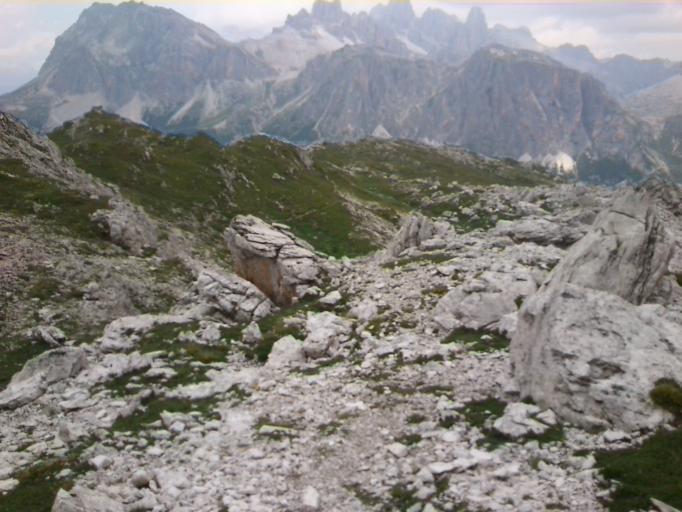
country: IT
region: Veneto
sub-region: Provincia di Belluno
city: Selva di Cadore
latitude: 46.5026
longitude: 12.0336
